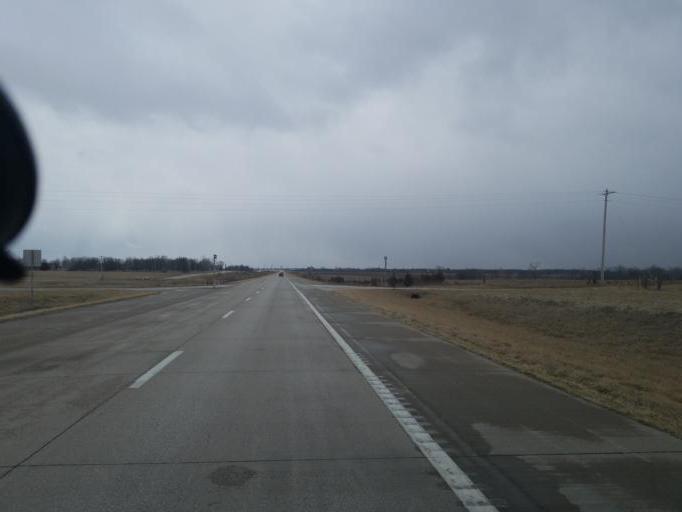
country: US
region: Missouri
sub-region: Randolph County
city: Moberly
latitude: 39.4835
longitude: -92.4347
